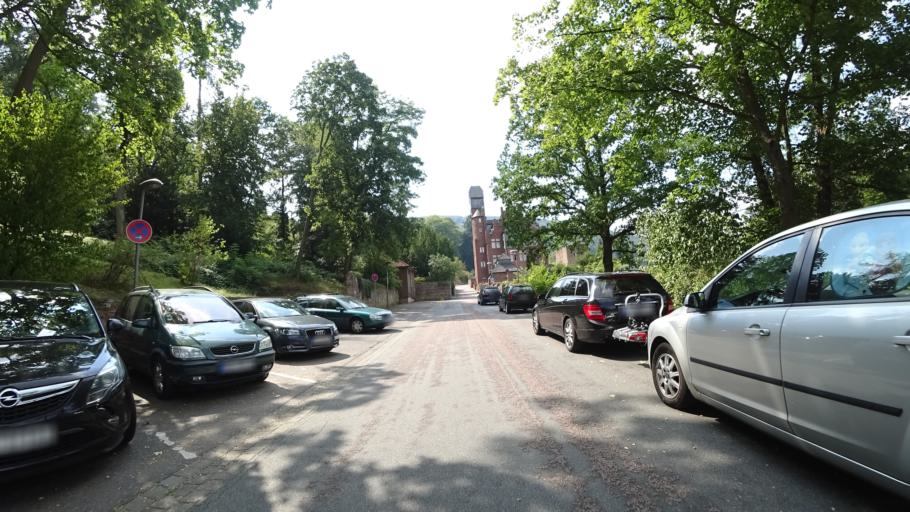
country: DE
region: Bavaria
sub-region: Regierungsbezirk Unterfranken
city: Miltenberg
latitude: 49.6994
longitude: 9.2564
